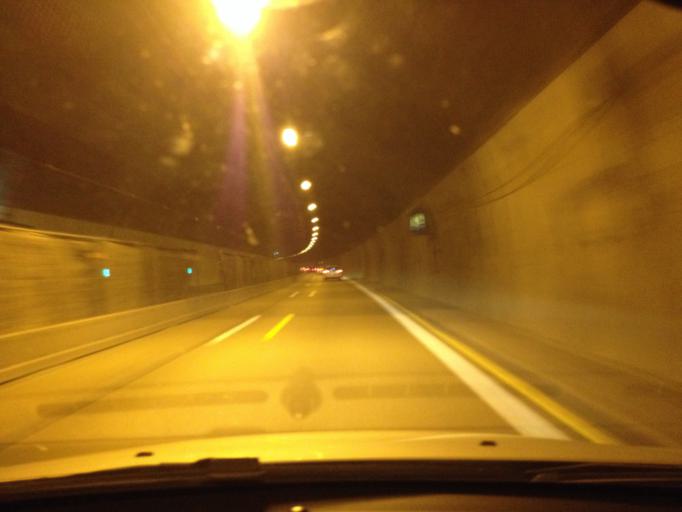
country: DE
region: Baden-Wuerttemberg
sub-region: Regierungsbezirk Stuttgart
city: Westhausen
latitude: 48.8734
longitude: 10.1680
